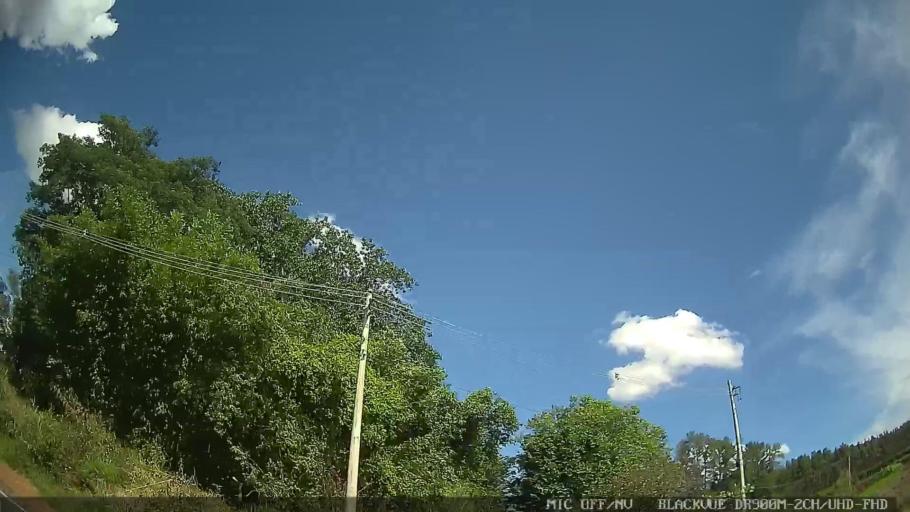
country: BR
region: Sao Paulo
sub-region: Pedreira
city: Pedreira
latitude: -22.7263
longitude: -46.8523
